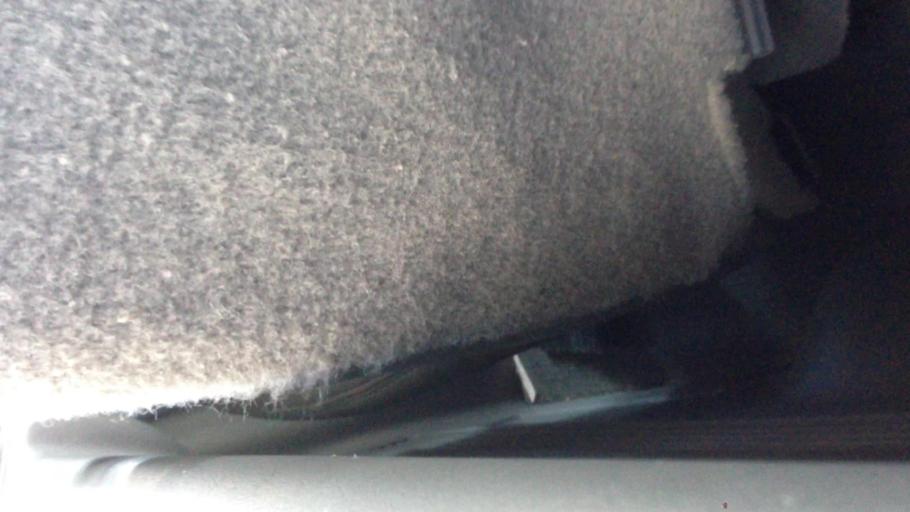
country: US
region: New York
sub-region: Columbia County
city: Hudson
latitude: 42.2031
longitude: -73.7995
